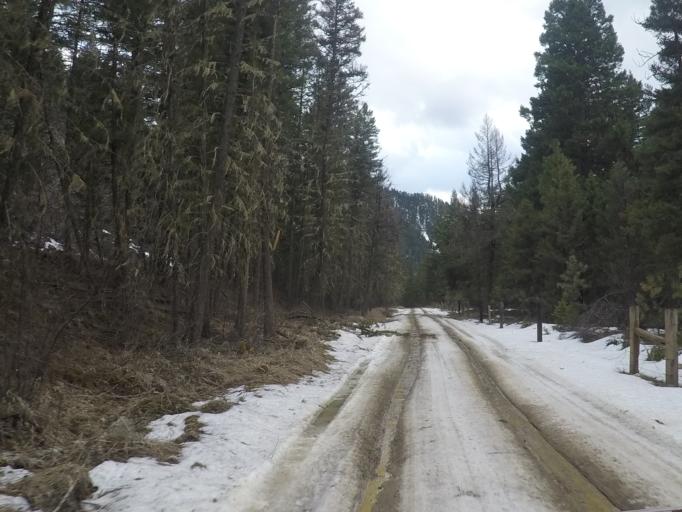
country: US
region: Montana
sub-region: Missoula County
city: Clinton
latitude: 46.5774
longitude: -113.6823
